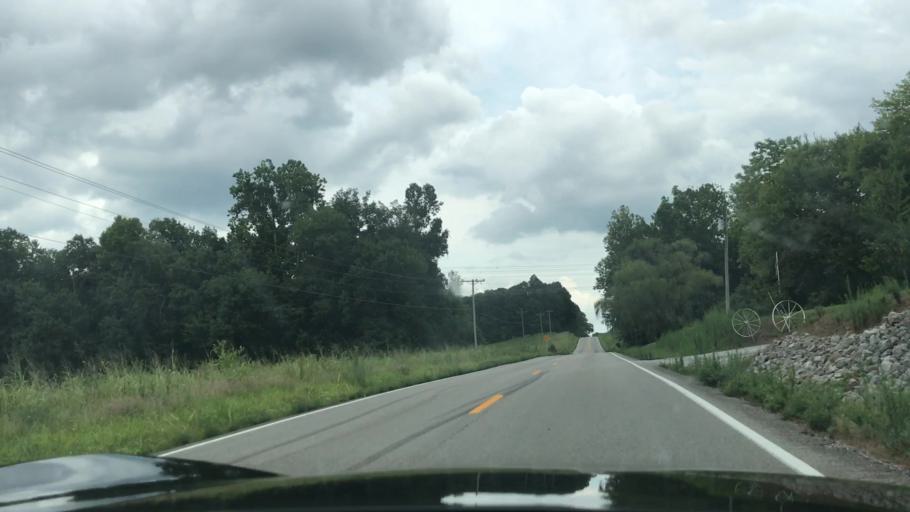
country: US
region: Kentucky
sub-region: Muhlenberg County
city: Central City
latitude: 37.1996
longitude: -87.0031
